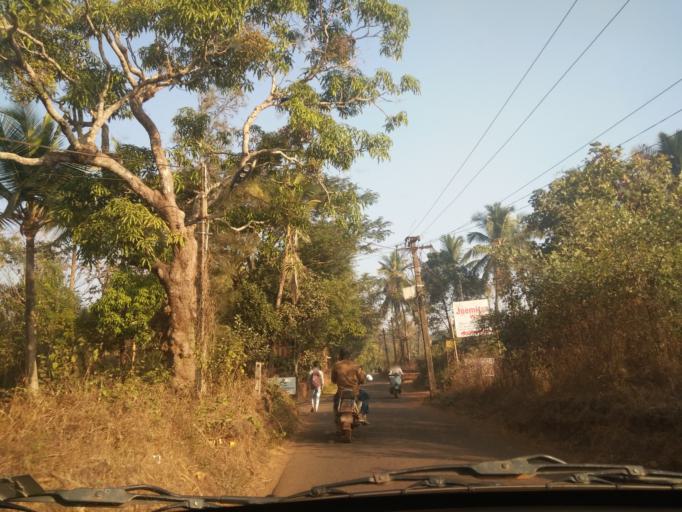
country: IN
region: Goa
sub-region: South Goa
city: Davorlim
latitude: 15.2851
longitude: 74.0067
